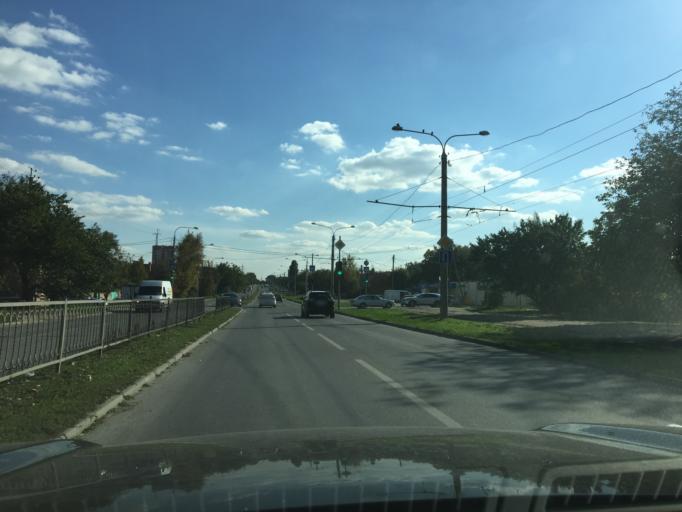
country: RU
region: Rostov
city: Rostov-na-Donu
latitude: 47.2221
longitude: 39.6440
